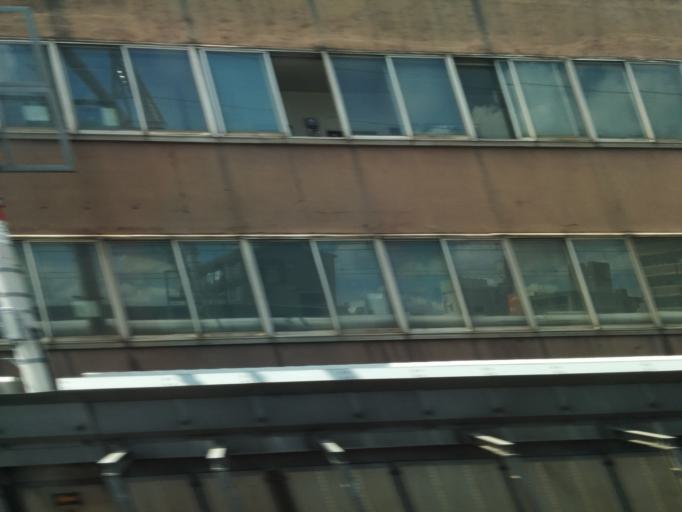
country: JP
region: Aichi
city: Nagoya-shi
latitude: 35.1230
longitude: 136.8886
